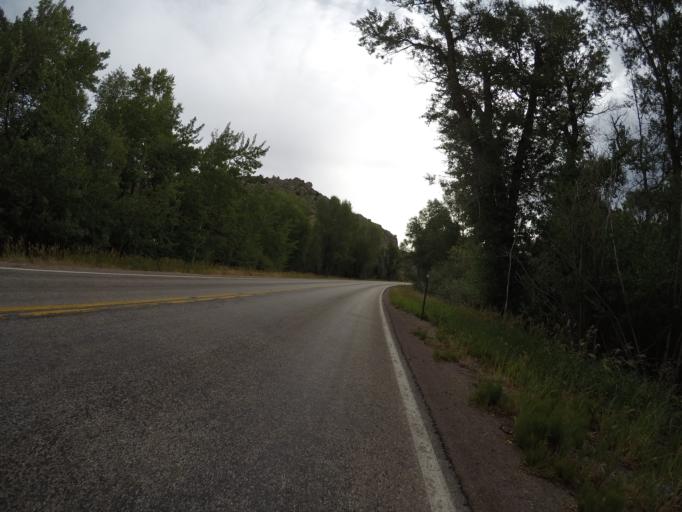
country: US
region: Wyoming
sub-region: Carbon County
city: Saratoga
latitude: 41.3589
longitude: -106.5716
